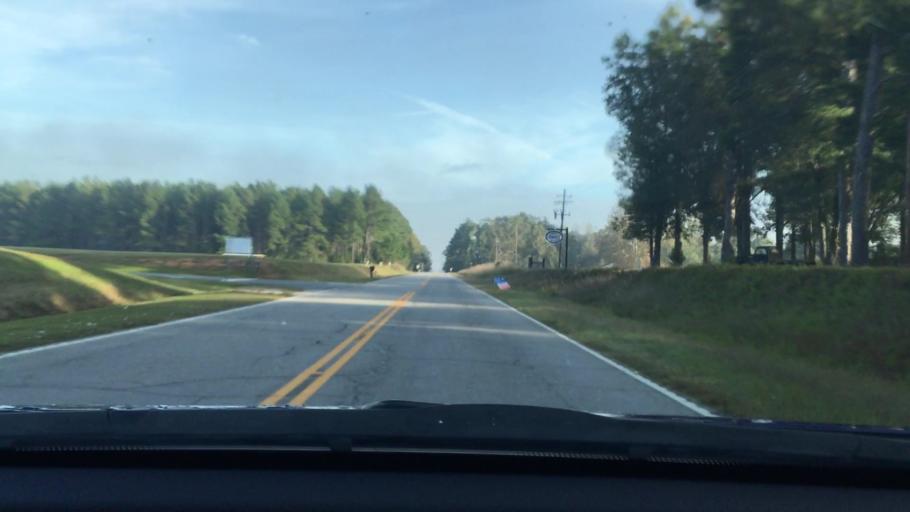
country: US
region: South Carolina
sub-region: Sumter County
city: East Sumter
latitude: 33.9714
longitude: -80.3000
